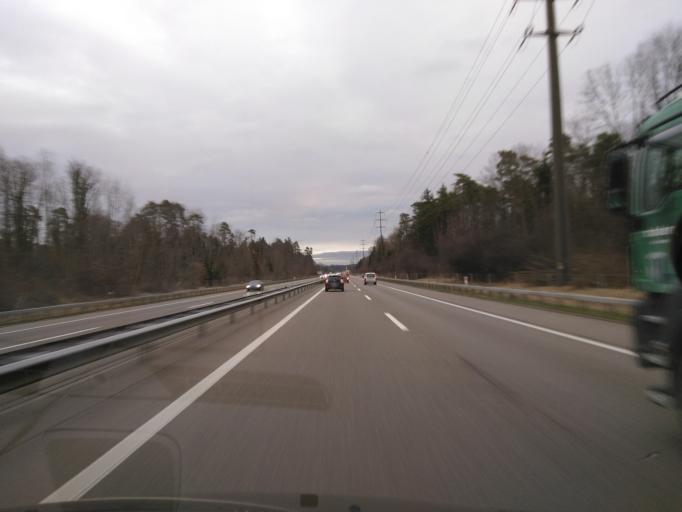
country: CH
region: Saint Gallen
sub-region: Wahlkreis Wil
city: Wil
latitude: 47.4560
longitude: 9.0691
